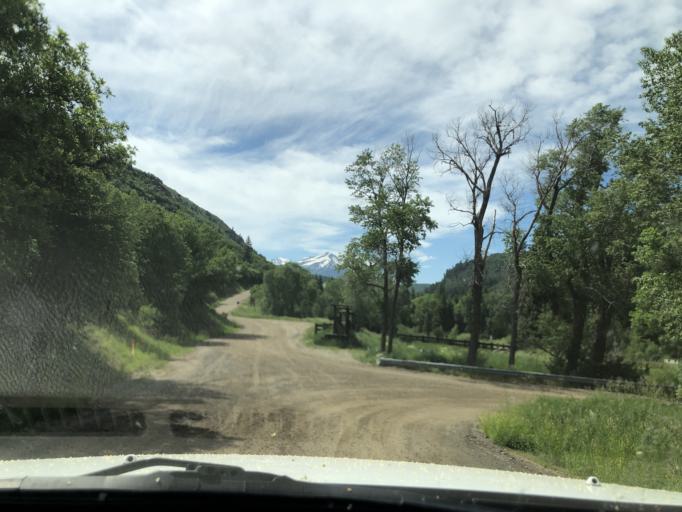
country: US
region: Colorado
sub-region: Delta County
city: Paonia
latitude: 38.9900
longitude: -107.3486
